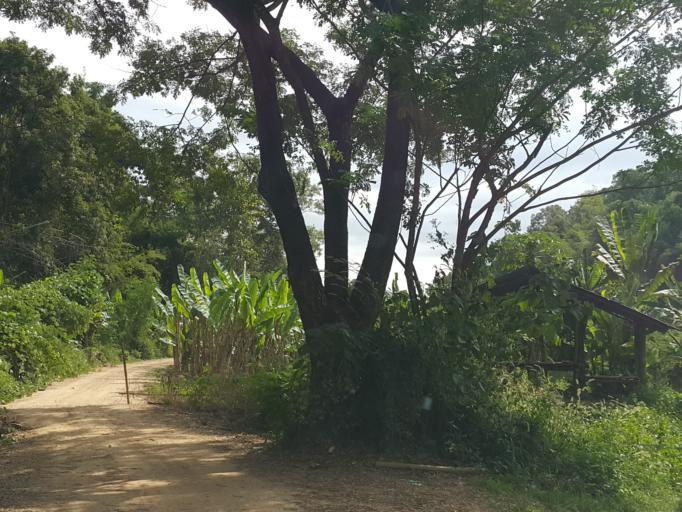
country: TH
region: Lampang
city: Hang Chat
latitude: 18.4898
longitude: 99.3986
